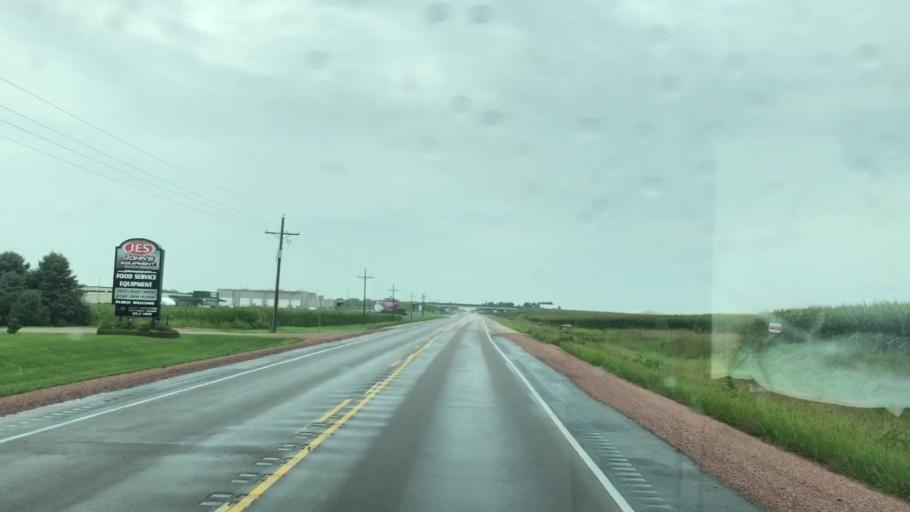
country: US
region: Iowa
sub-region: O'Brien County
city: Sheldon
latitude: 43.1861
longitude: -95.8039
